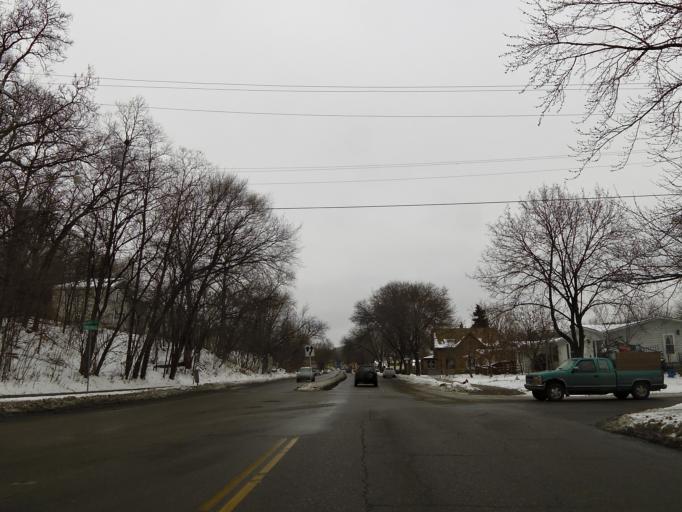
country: US
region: Minnesota
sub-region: Ramsey County
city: Saint Paul
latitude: 44.9284
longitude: -93.0729
